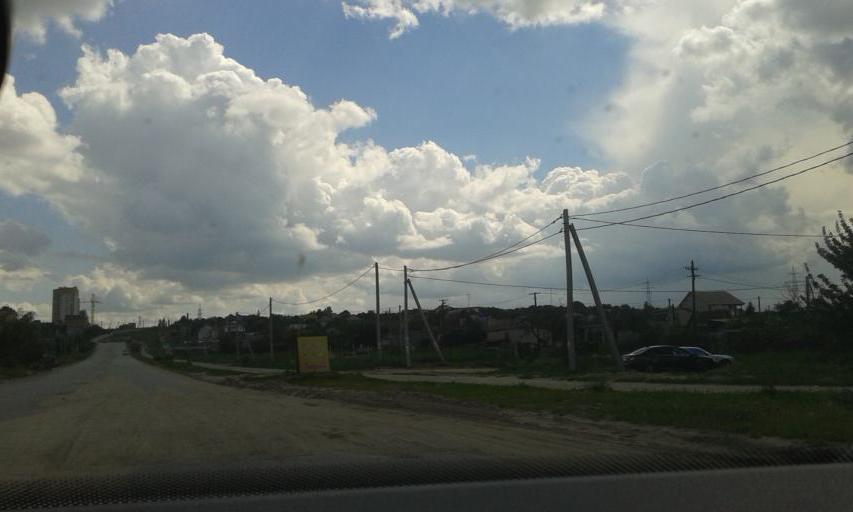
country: RU
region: Volgograd
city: Volgograd
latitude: 48.6551
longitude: 44.4133
